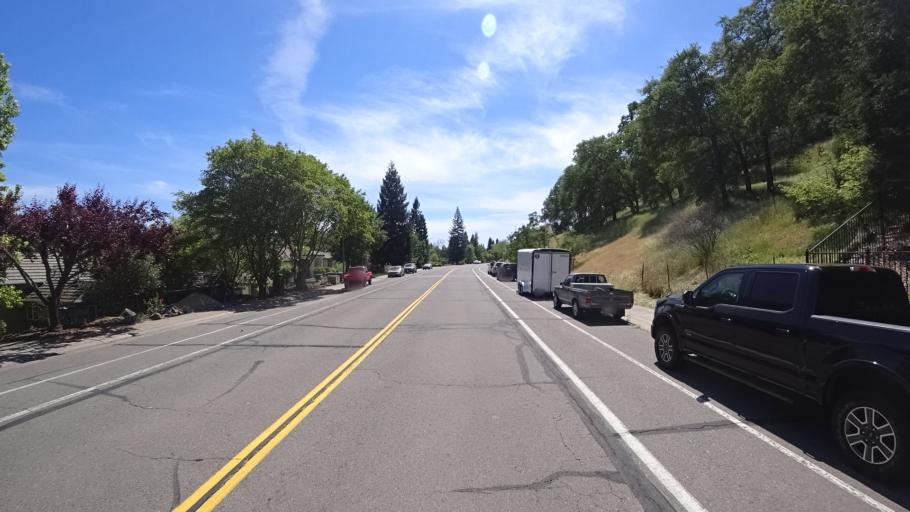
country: US
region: California
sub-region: Placer County
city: Rocklin
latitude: 38.8180
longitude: -121.2356
